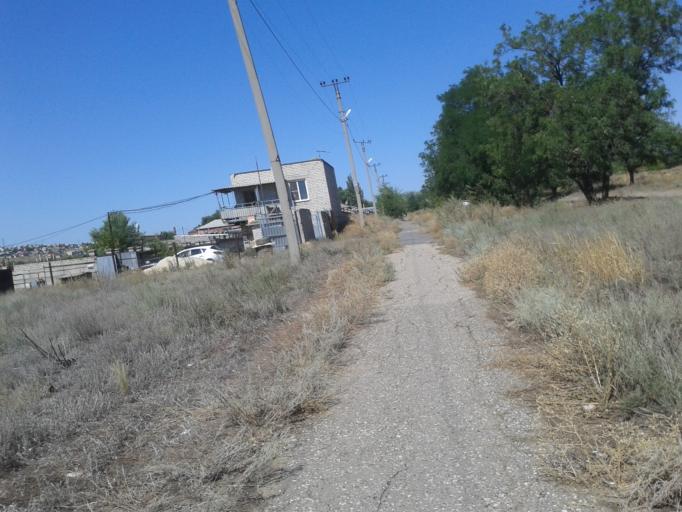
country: RU
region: Volgograd
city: Volgograd
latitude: 48.6894
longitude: 44.4494
